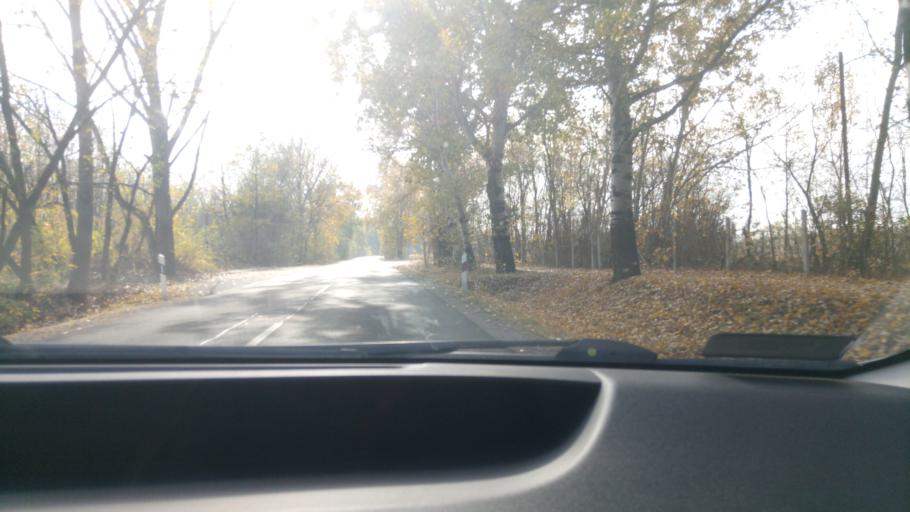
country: HU
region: Bacs-Kiskun
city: Jaszszentlaszlo
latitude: 46.5546
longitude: 19.7478
